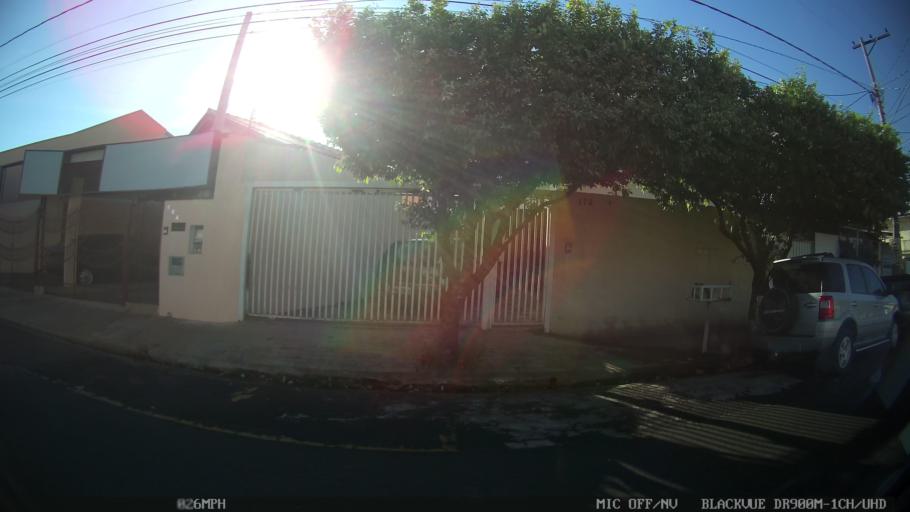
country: BR
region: Sao Paulo
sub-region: Sao Jose Do Rio Preto
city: Sao Jose do Rio Preto
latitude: -20.8114
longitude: -49.3968
